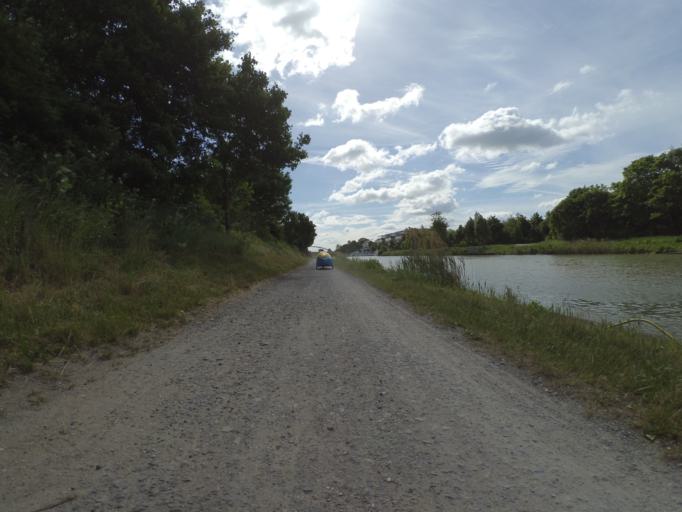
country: DE
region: Lower Saxony
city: Hannover
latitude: 52.4070
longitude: 9.7429
